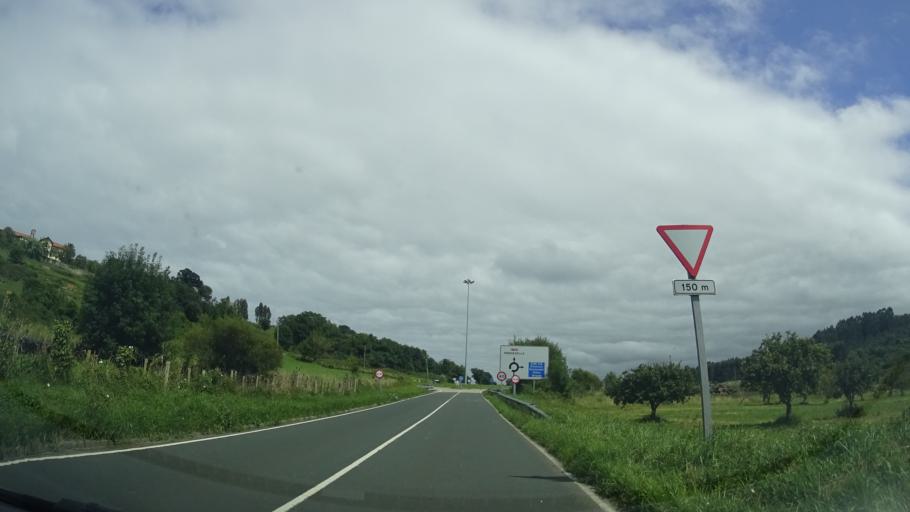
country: ES
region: Asturias
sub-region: Province of Asturias
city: Ribadesella
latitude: 43.4649
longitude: -5.1206
